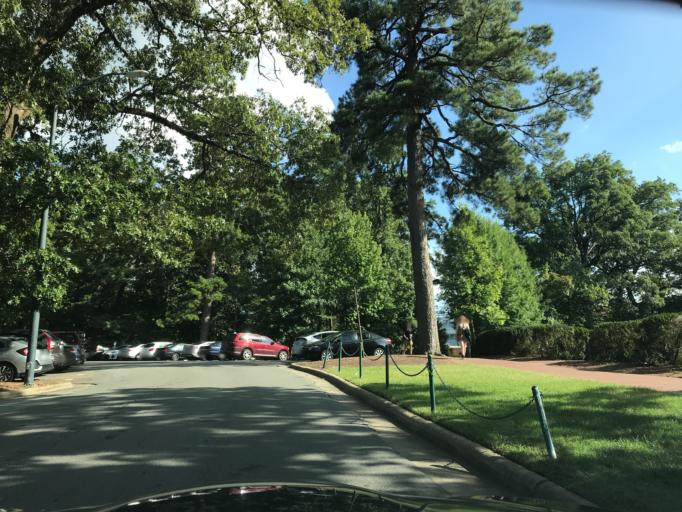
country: US
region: North Carolina
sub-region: Orange County
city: Chapel Hill
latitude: 35.9091
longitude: -79.0487
